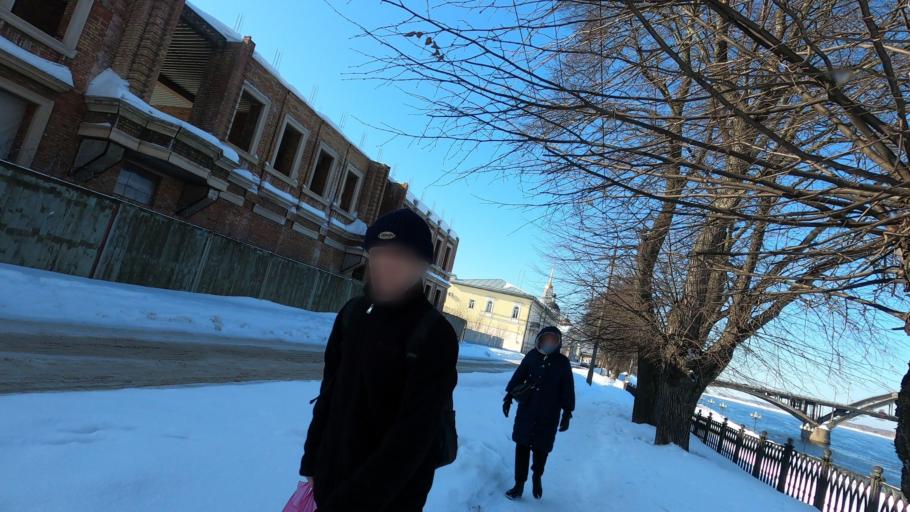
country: RU
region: Jaroslavl
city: Rybinsk
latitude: 58.0475
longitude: 38.8651
